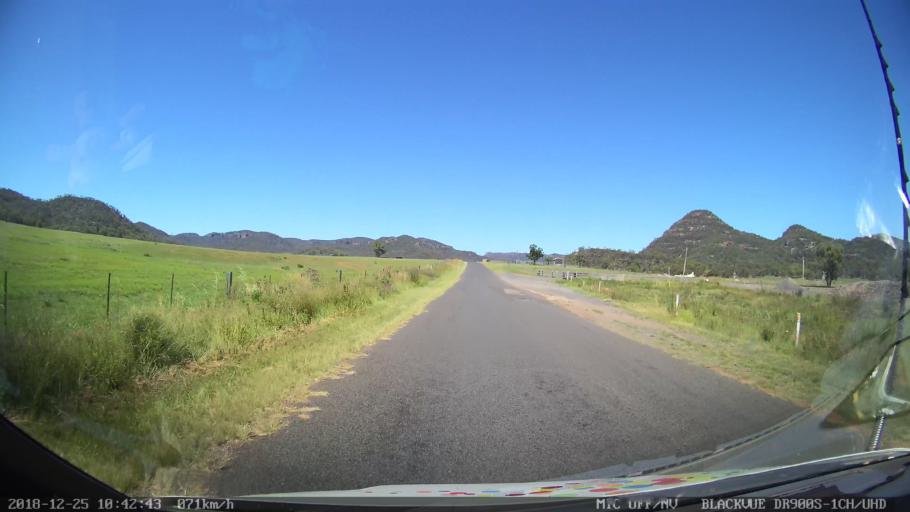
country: AU
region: New South Wales
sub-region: Upper Hunter Shire
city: Merriwa
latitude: -32.4173
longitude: 150.3203
